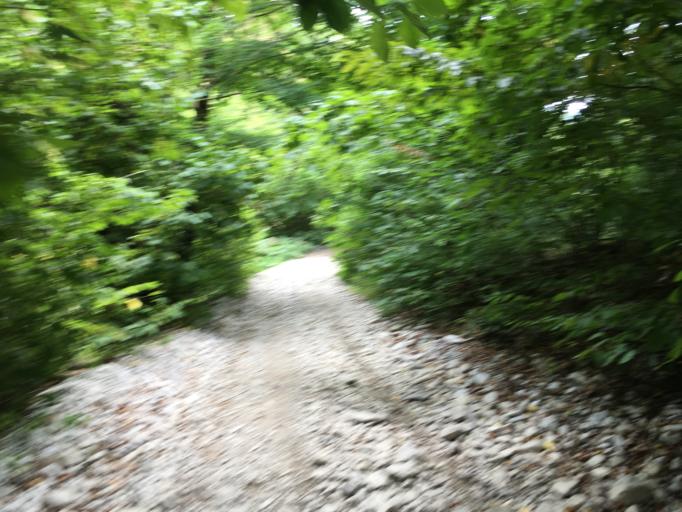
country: RU
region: Krasnodarskiy
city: Tuapse
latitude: 44.2637
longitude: 39.2141
